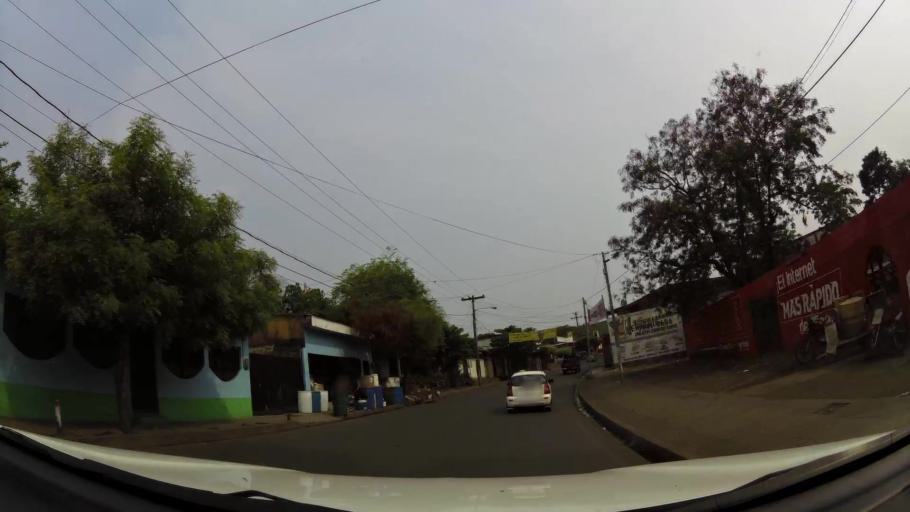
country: NI
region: Chinandega
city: Chinandega
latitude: 12.6344
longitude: -87.1352
